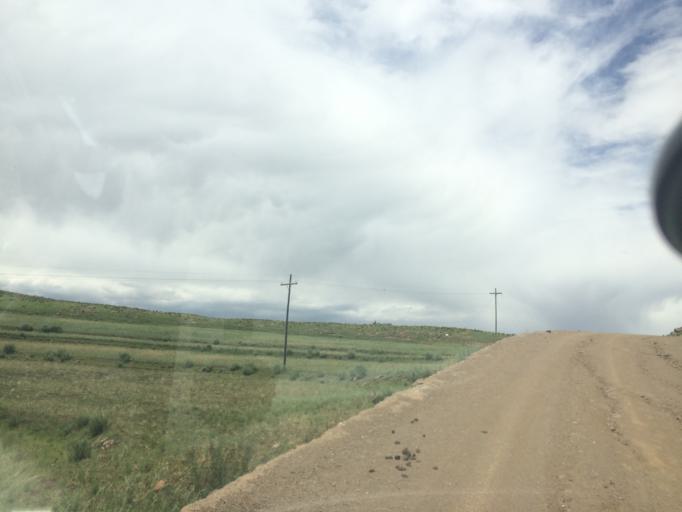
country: LS
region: Maseru
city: Nako
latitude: -29.8682
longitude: 28.0395
